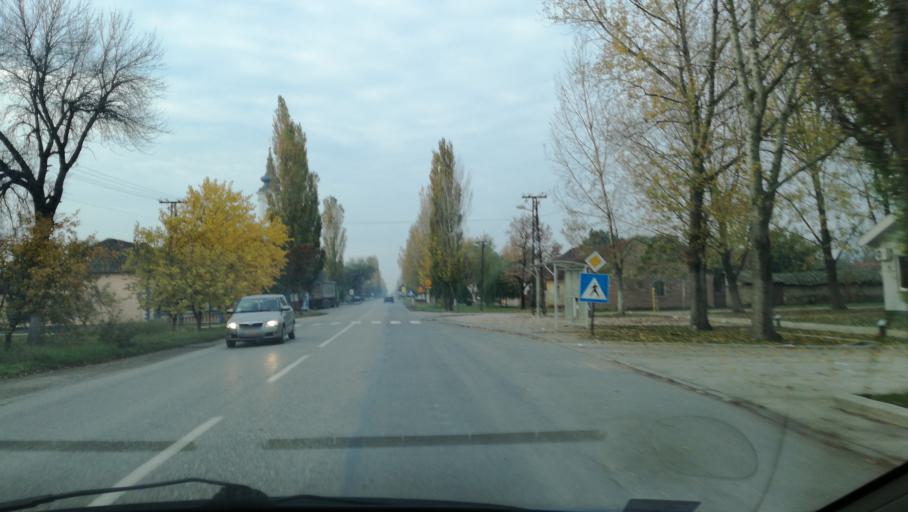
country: RS
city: Basaid
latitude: 45.6444
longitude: 20.4164
